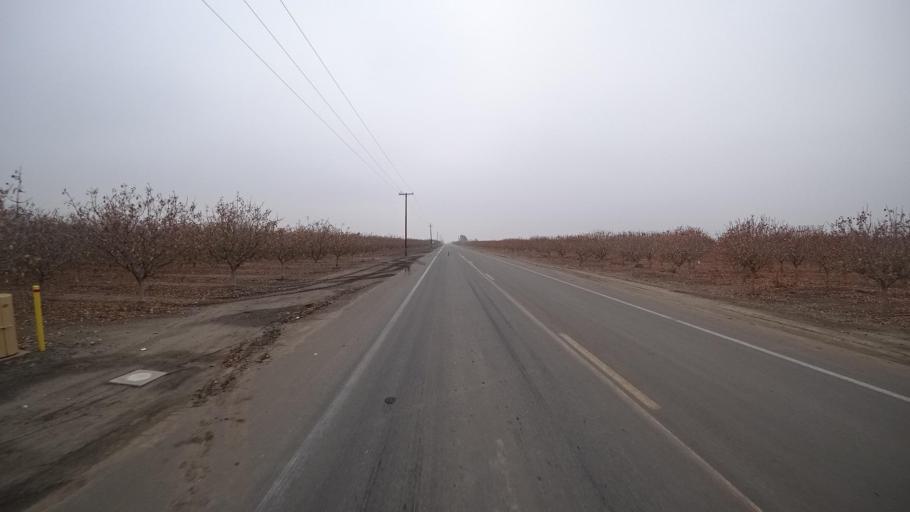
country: US
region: California
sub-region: Kern County
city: Buttonwillow
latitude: 35.3693
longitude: -119.4481
